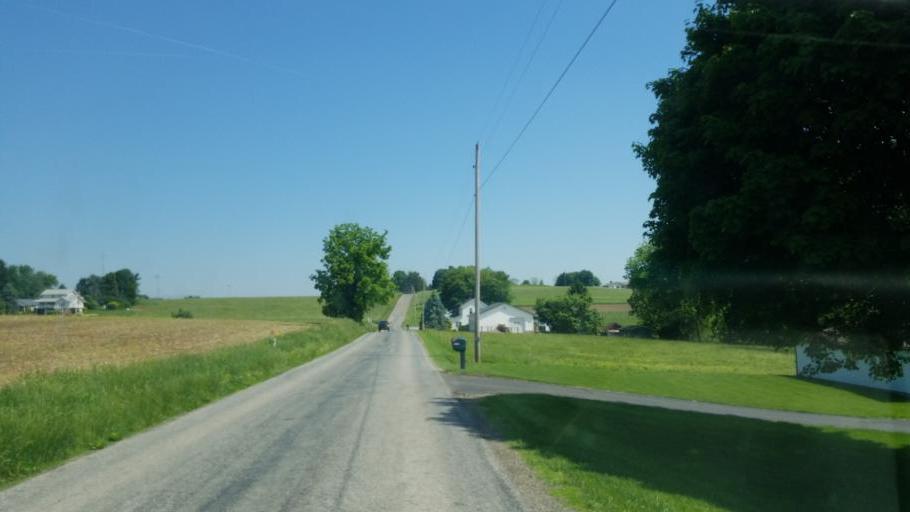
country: US
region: Ohio
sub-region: Holmes County
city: Millersburg
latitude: 40.5423
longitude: -81.7777
